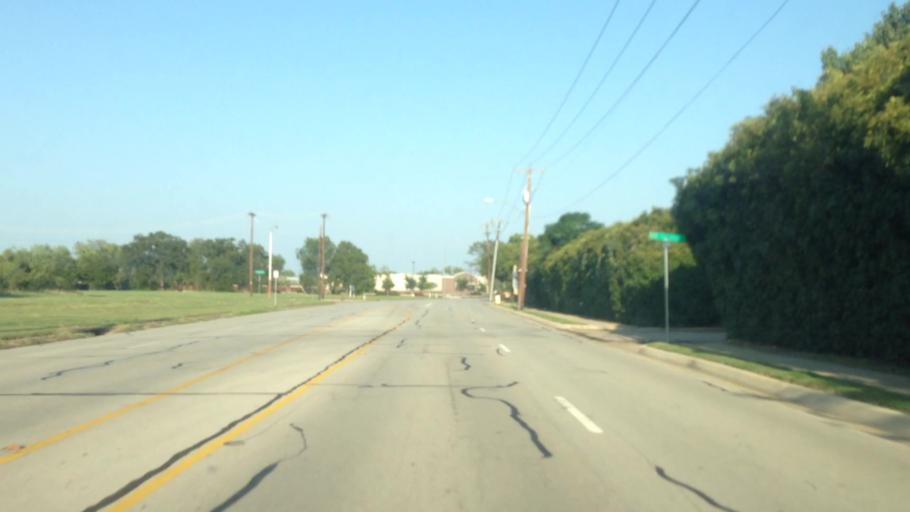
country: US
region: Texas
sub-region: Tarrant County
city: Pantego
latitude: 32.7536
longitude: -97.1766
